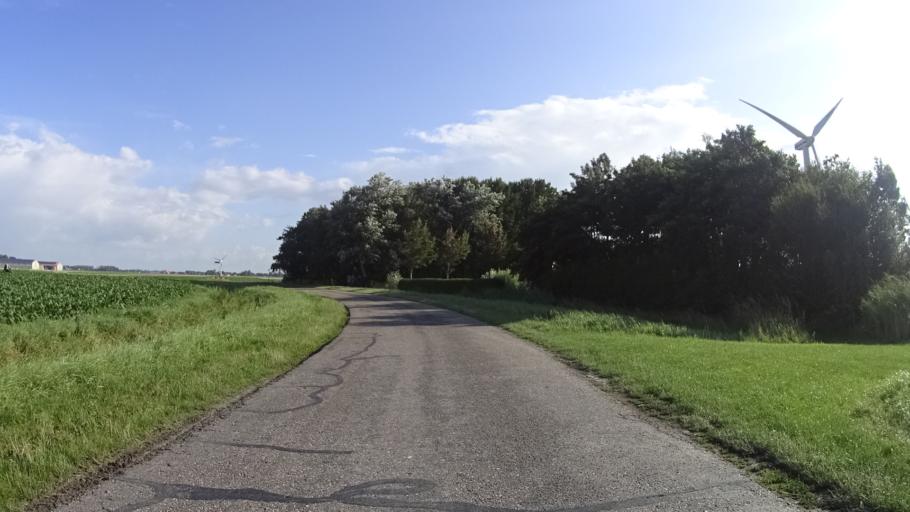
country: NL
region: Friesland
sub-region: Gemeente Harlingen
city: Harlingen
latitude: 53.1220
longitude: 5.4316
